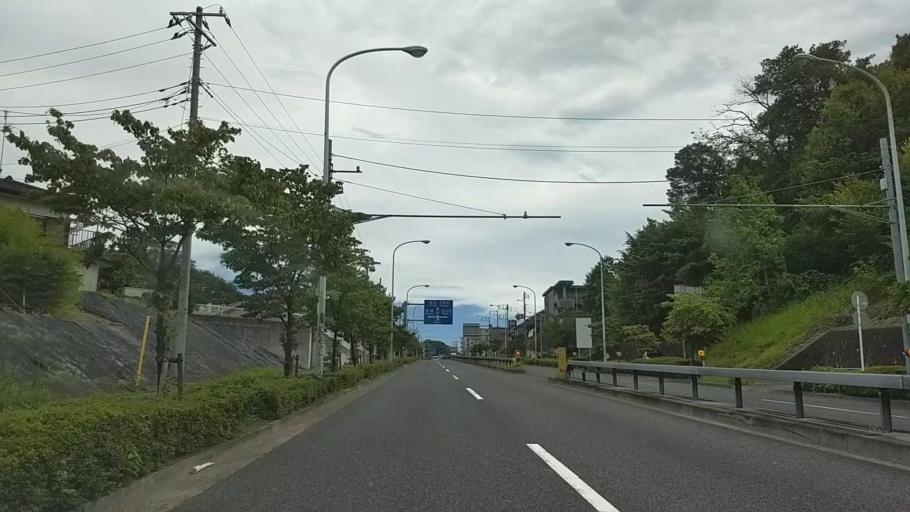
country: JP
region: Tokyo
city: Hachioji
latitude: 35.6421
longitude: 139.3568
